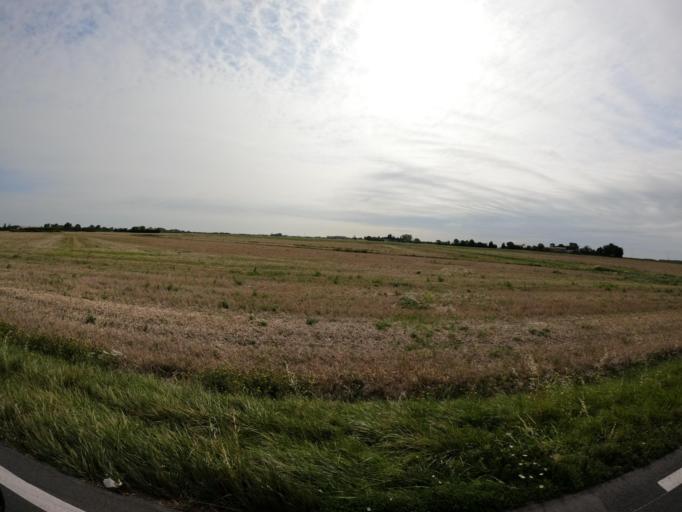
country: FR
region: Pays de la Loire
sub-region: Departement de la Vendee
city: Triaize
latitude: 46.3782
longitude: -1.2031
